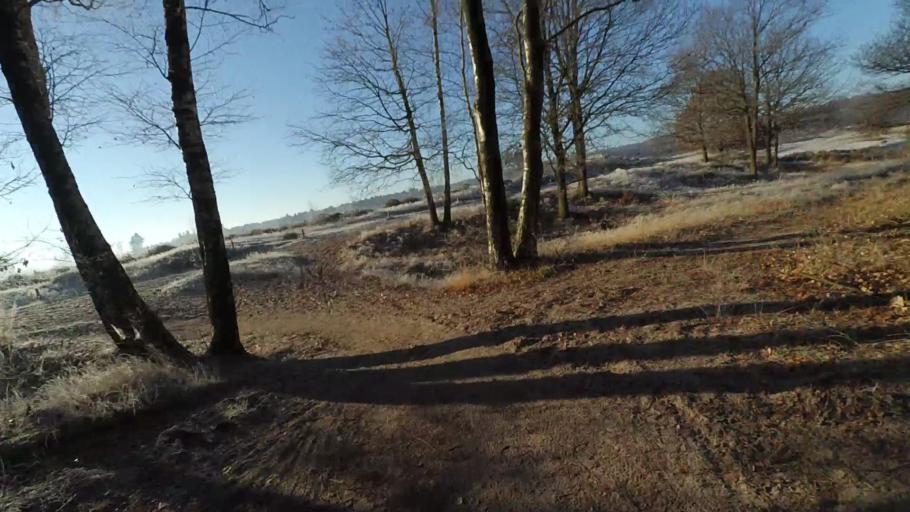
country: NL
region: Utrecht
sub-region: Gemeente Utrechtse Heuvelrug
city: Maarn
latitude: 52.0993
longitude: 5.3686
